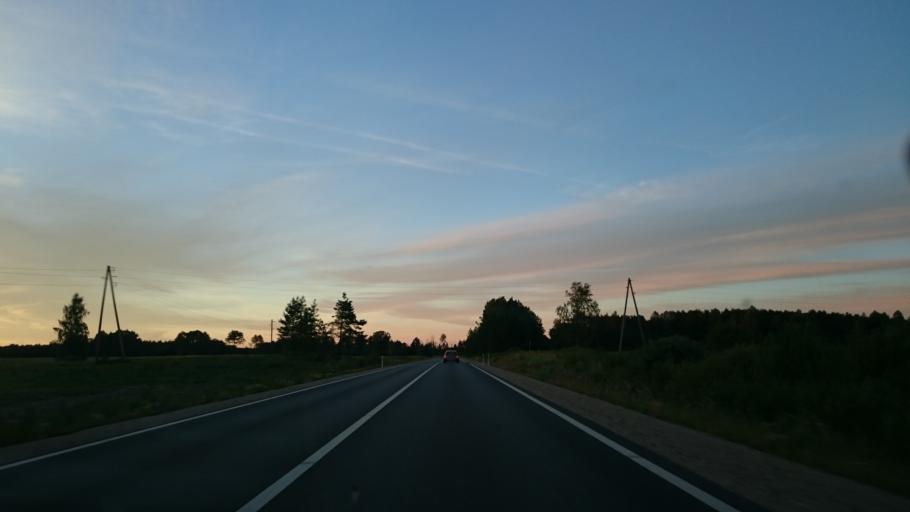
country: LV
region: Dobeles Rajons
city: Dobele
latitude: 56.7129
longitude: 23.1884
